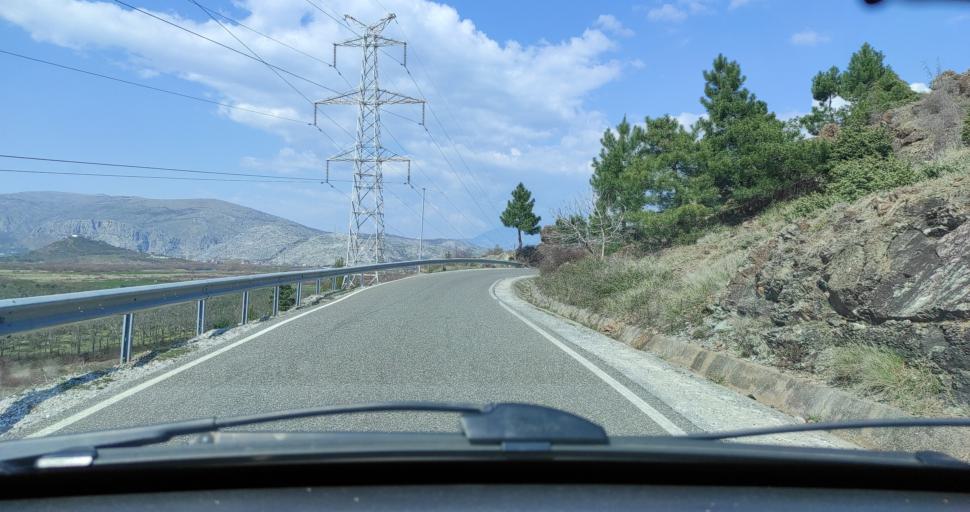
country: AL
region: Shkoder
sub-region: Rrethi i Shkodres
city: Vau i Dejes
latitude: 41.9868
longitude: 19.6432
